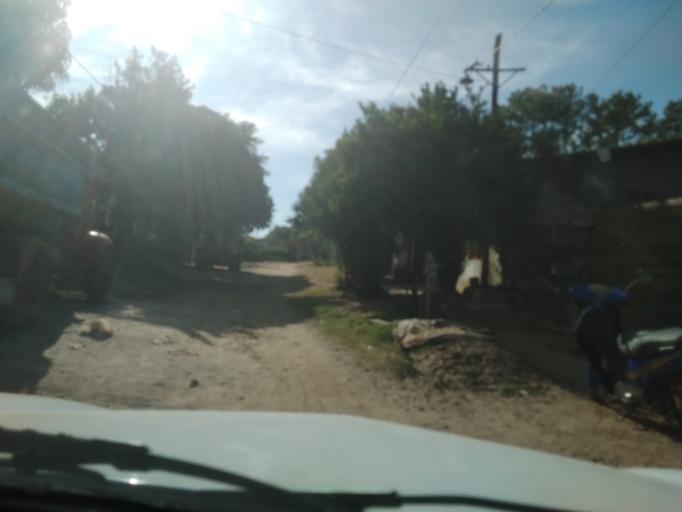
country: AR
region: Corrientes
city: Corrientes
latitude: -27.5067
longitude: -58.8050
